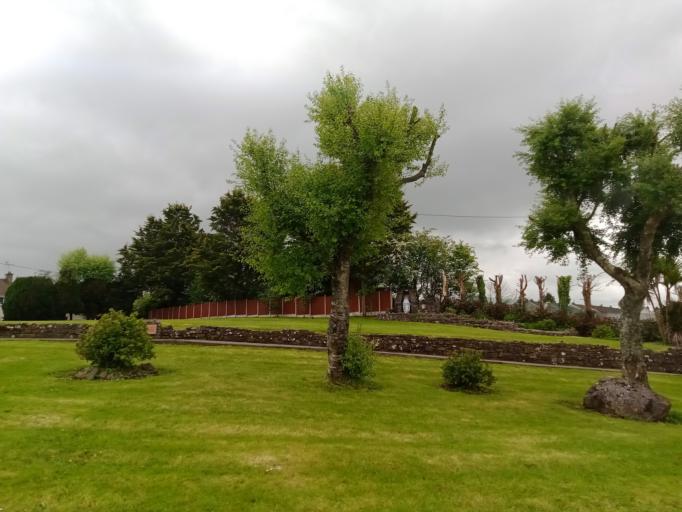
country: IE
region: Munster
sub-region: County Cork
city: Bandon
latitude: 51.7442
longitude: -8.7264
